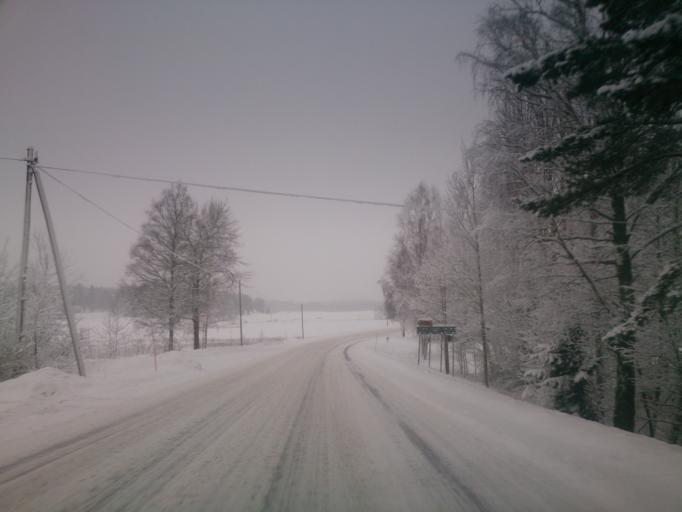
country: SE
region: OEstergoetland
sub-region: Finspangs Kommun
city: Finspang
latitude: 58.6669
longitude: 15.7649
